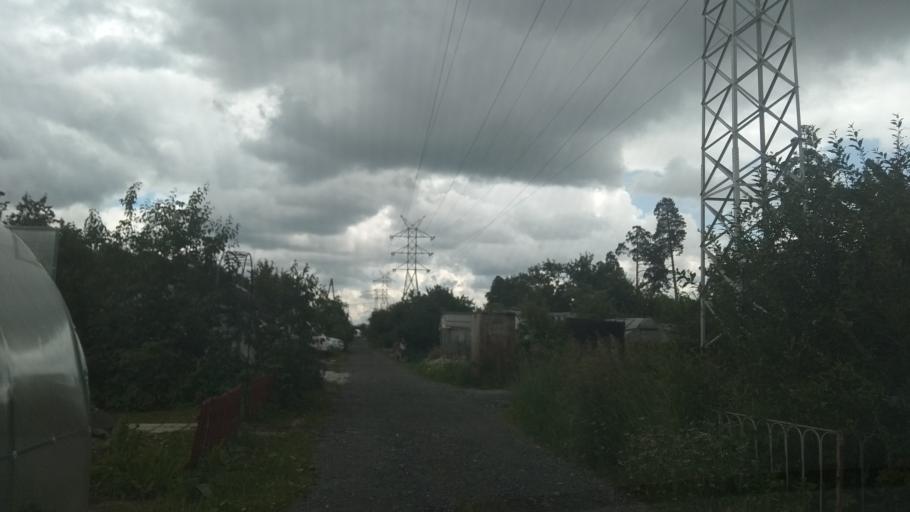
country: RU
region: Sverdlovsk
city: Verkhnyaya Pyshma
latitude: 56.9207
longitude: 60.5733
